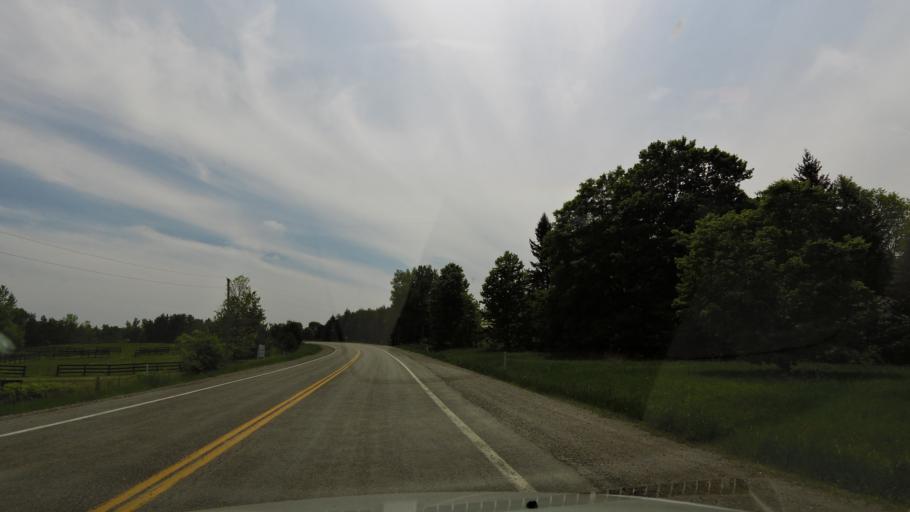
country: CA
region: Ontario
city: Omemee
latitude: 43.9737
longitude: -78.5076
